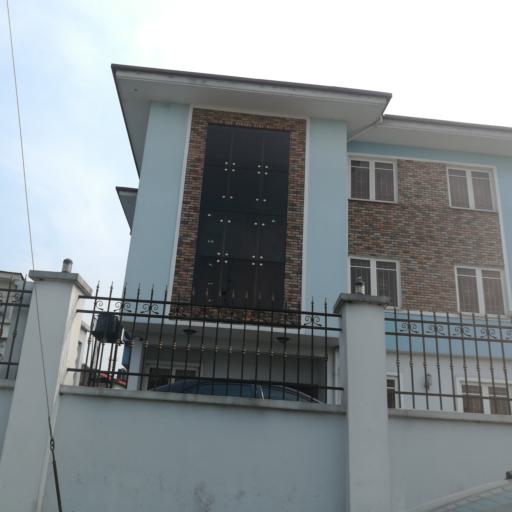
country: NG
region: Rivers
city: Port Harcourt
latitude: 4.8454
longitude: 7.0473
